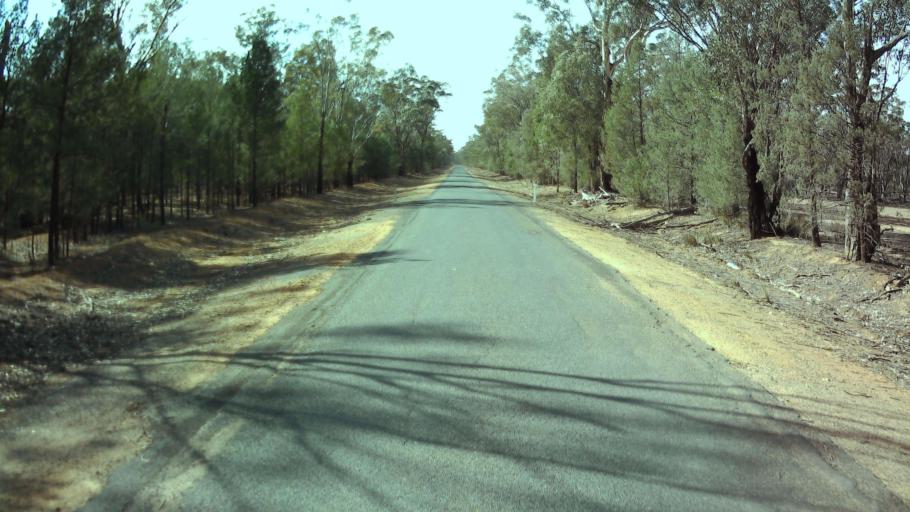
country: AU
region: New South Wales
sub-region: Weddin
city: Grenfell
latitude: -33.7142
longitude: 148.0244
